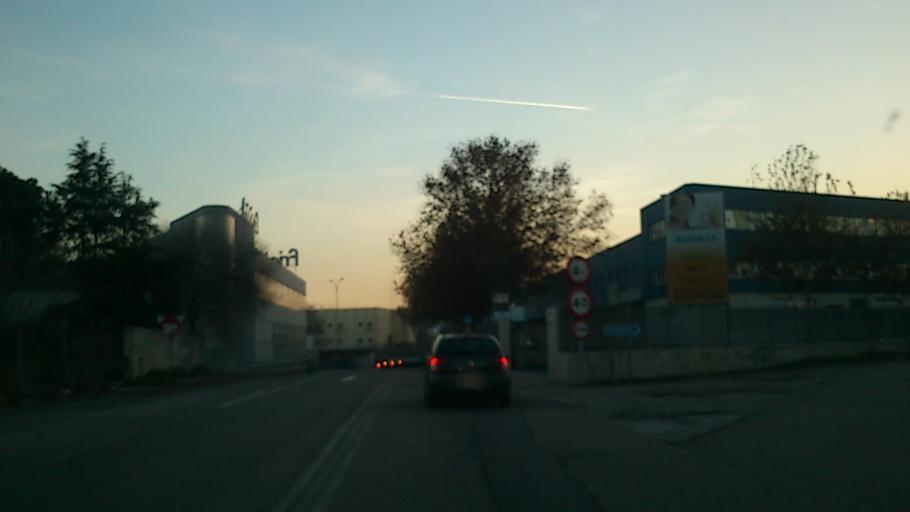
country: ES
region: Madrid
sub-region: Provincia de Madrid
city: San Fernando de Henares
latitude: 40.4441
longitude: -3.5411
